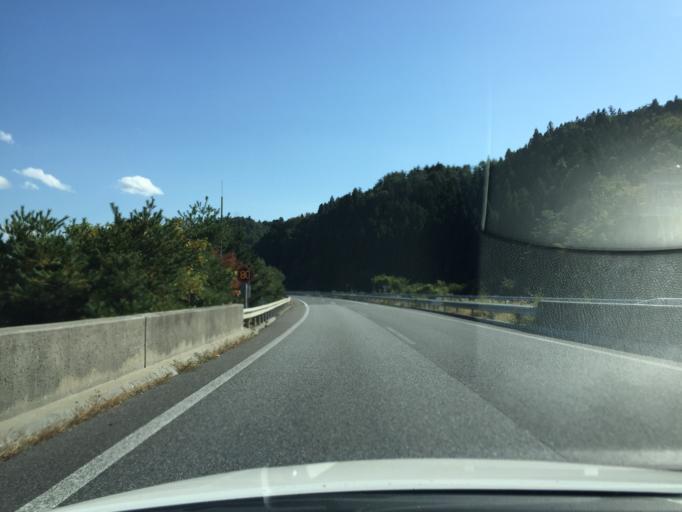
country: JP
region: Fukushima
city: Iwaki
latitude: 37.1151
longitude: 140.7520
